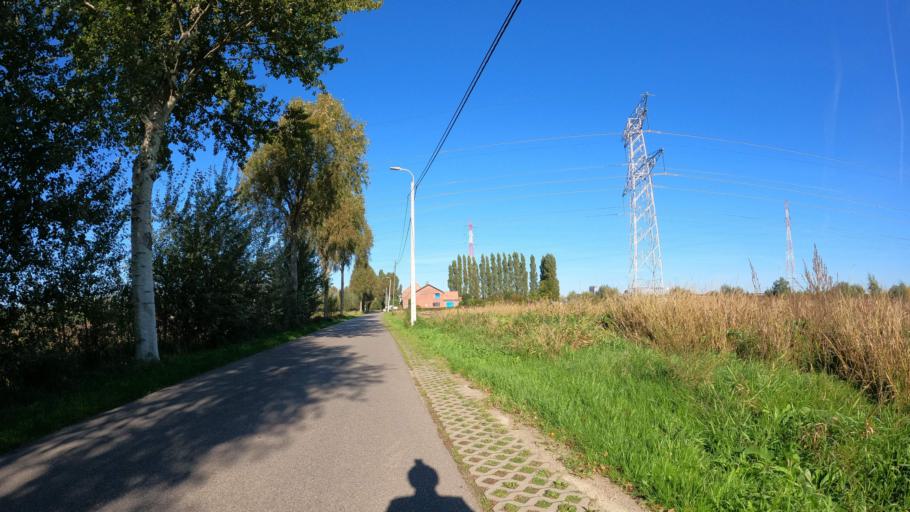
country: BE
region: Flanders
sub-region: Provincie Oost-Vlaanderen
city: Sint-Niklaas
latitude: 51.1372
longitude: 4.1669
